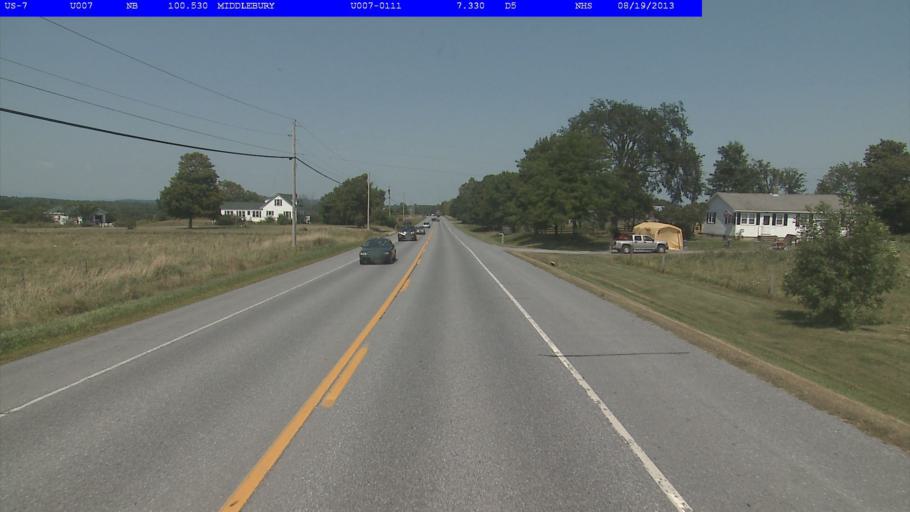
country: US
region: Vermont
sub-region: Addison County
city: Middlebury (village)
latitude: 44.0448
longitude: -73.1628
